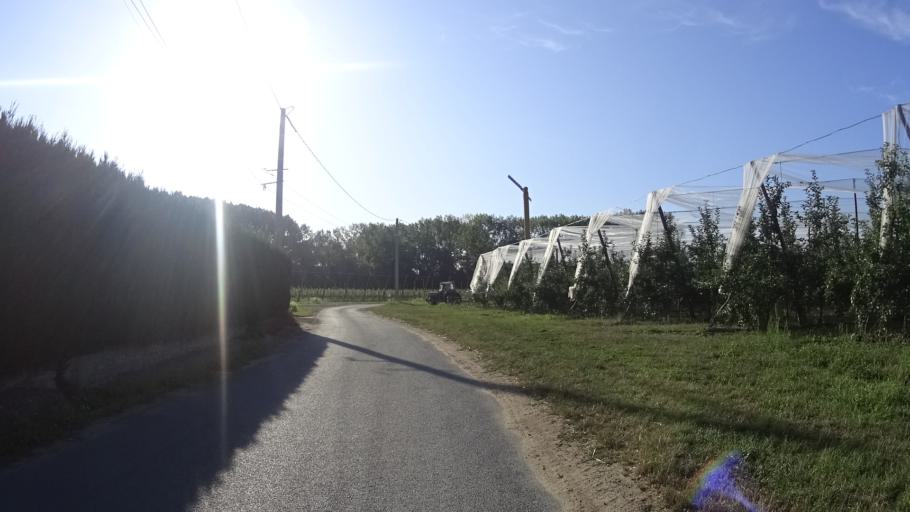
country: FR
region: Pays de la Loire
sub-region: Departement de Maine-et-Loire
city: Varennes-sur-Loire
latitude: 47.2585
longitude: 0.0270
